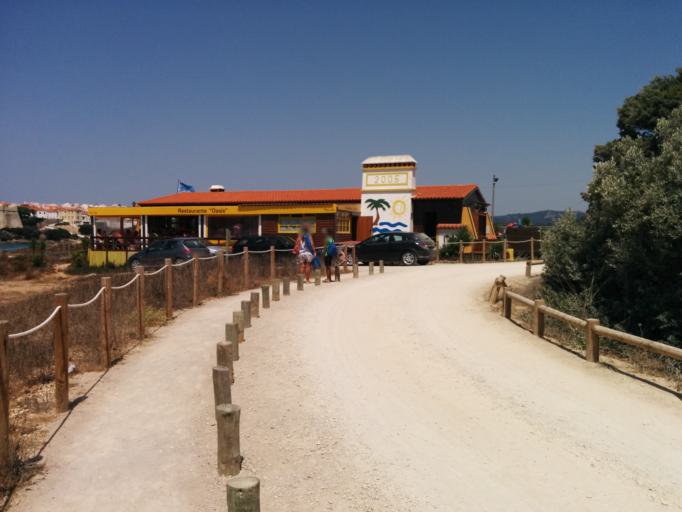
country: PT
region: Beja
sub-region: Odemira
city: Vila Nova de Milfontes
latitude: 37.7188
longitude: -8.7838
